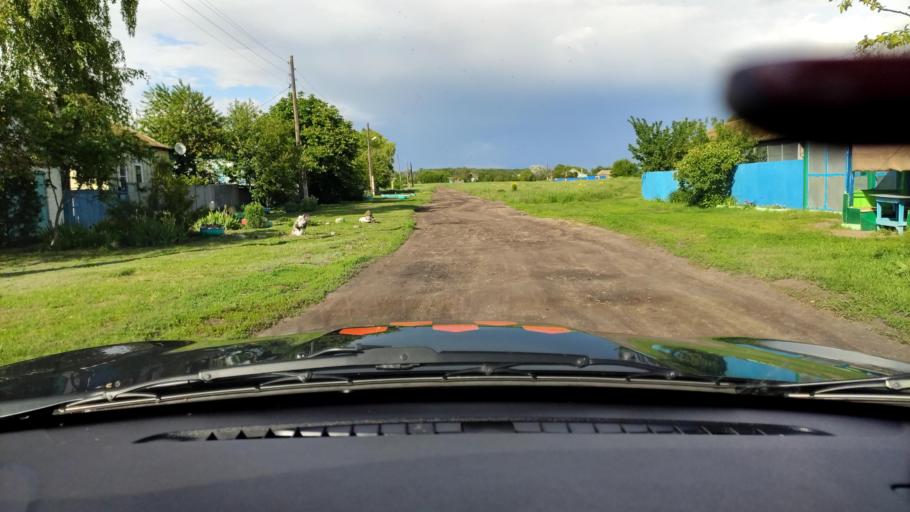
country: RU
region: Voronezj
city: Uryv-Pokrovka
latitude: 51.1150
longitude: 39.1807
